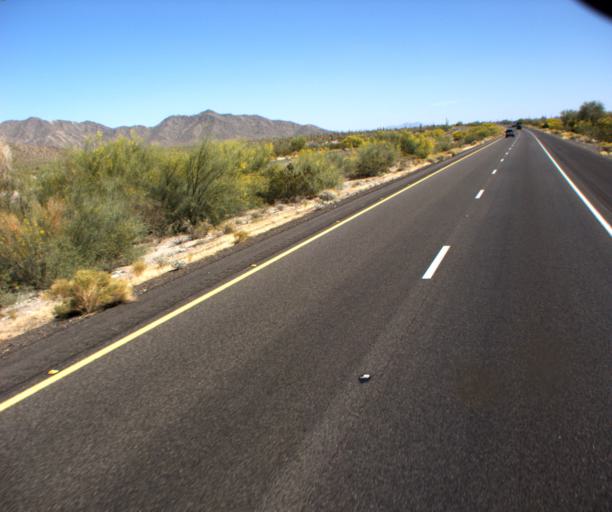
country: US
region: Arizona
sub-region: Maricopa County
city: Gila Bend
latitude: 32.8760
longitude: -112.4477
